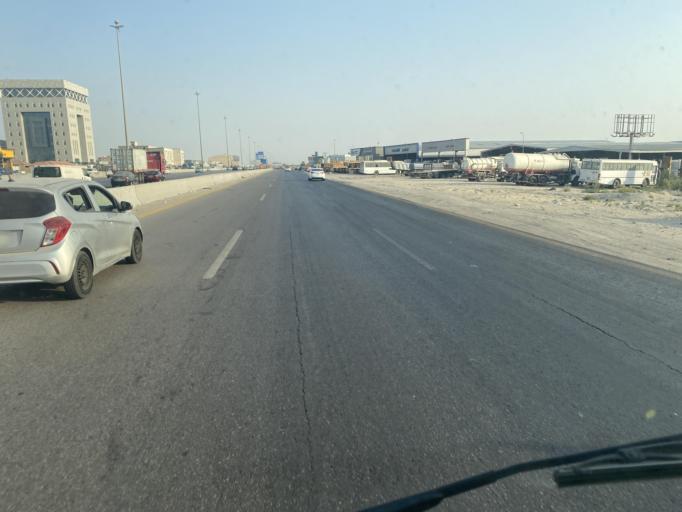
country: SA
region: Eastern Province
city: Sayhat
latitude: 26.4000
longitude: 50.0166
